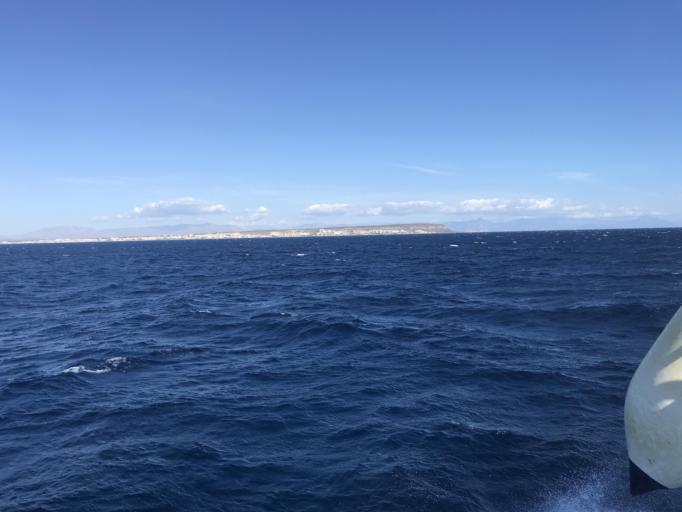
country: ES
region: Valencia
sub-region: Provincia de Alicante
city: Santa Pola
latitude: 38.1349
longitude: -0.5311
